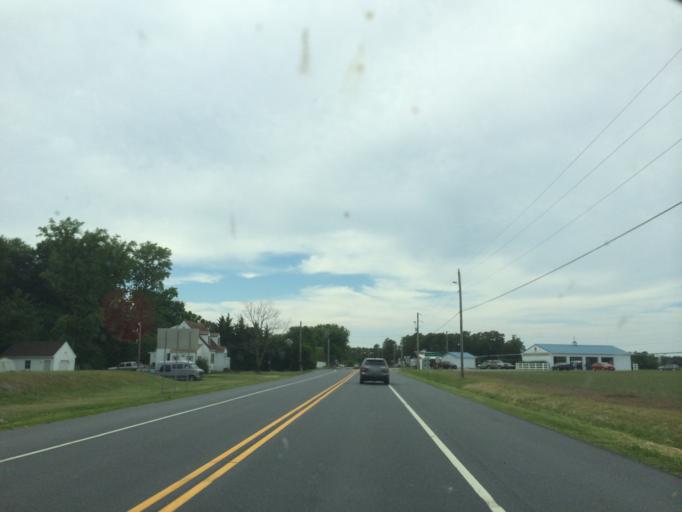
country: US
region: Delaware
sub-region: Sussex County
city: Bridgeville
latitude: 38.7796
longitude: -75.6658
